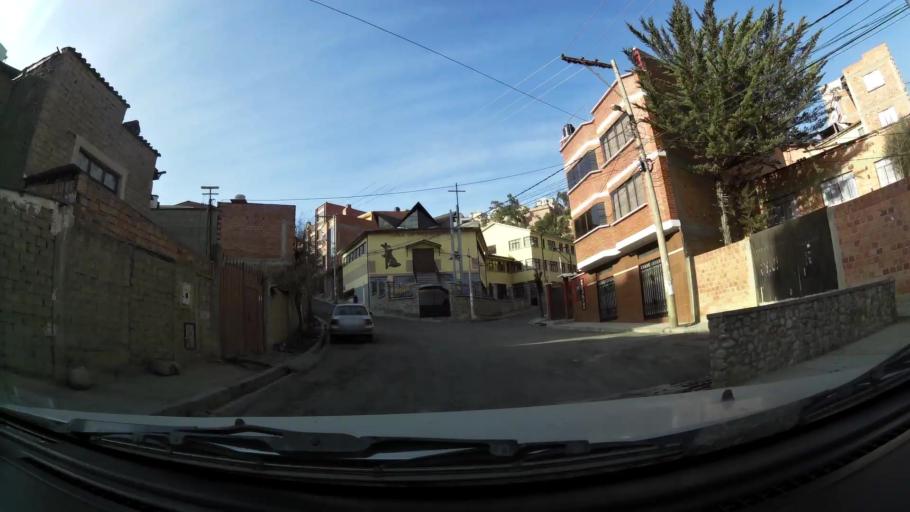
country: BO
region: La Paz
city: La Paz
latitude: -16.5309
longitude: -68.0950
